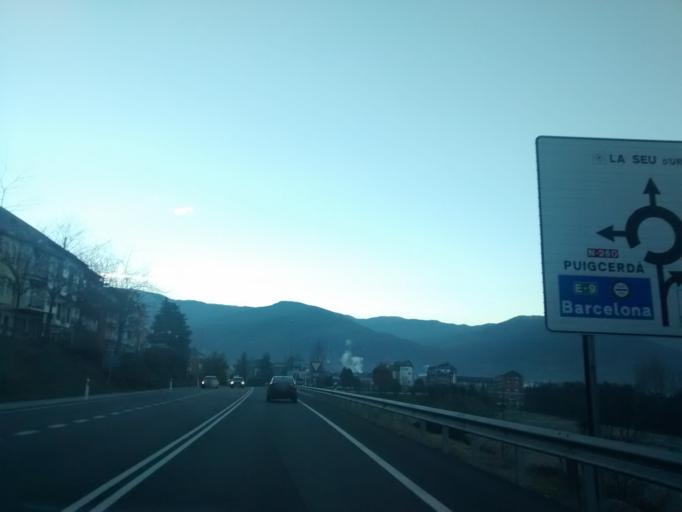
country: ES
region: Catalonia
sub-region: Provincia de Lleida
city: la Seu d'Urgell
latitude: 42.3645
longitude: 1.4554
